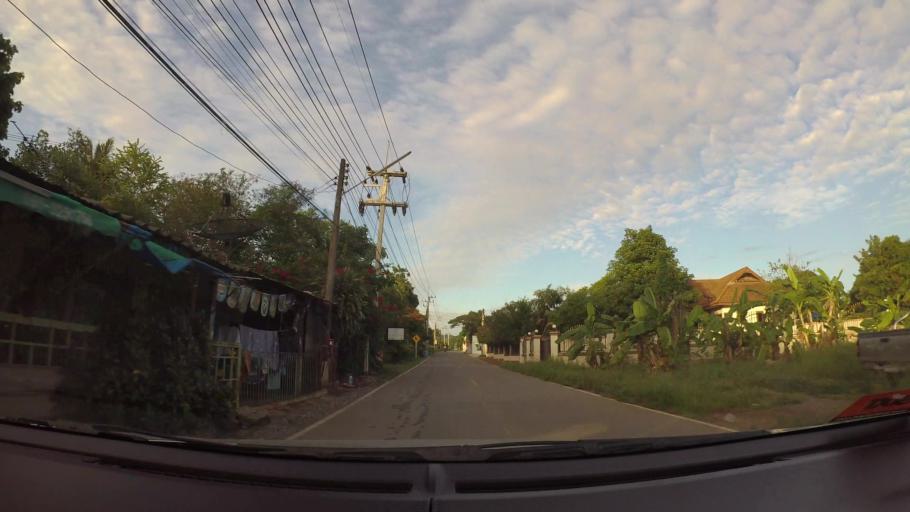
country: TH
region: Chon Buri
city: Sattahip
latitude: 12.7485
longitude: 100.9359
